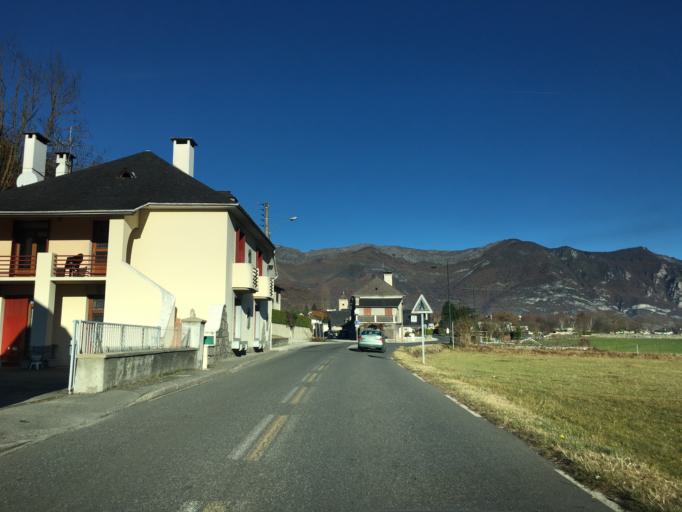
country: FR
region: Midi-Pyrenees
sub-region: Departement des Hautes-Pyrenees
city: Argeles-Gazost
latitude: 42.9940
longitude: -0.0914
